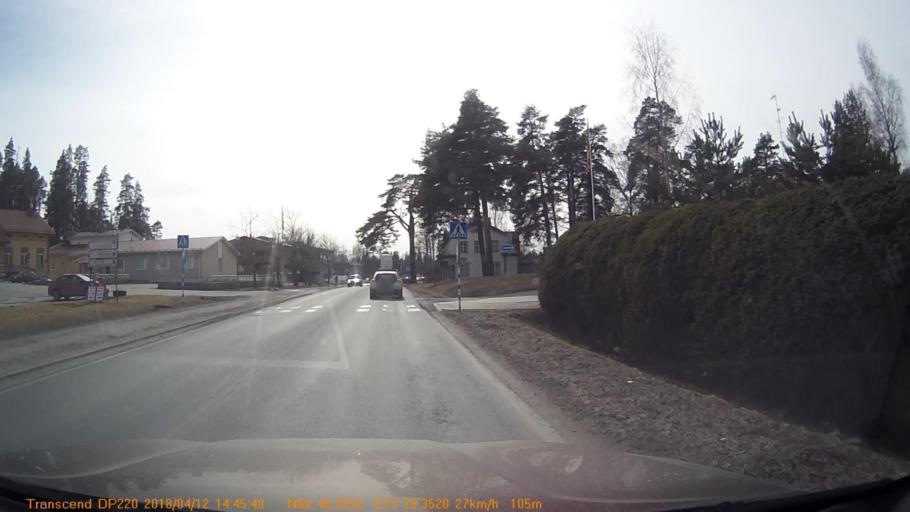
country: FI
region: Haeme
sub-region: Forssa
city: Jokioinen
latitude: 60.8053
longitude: 23.4890
